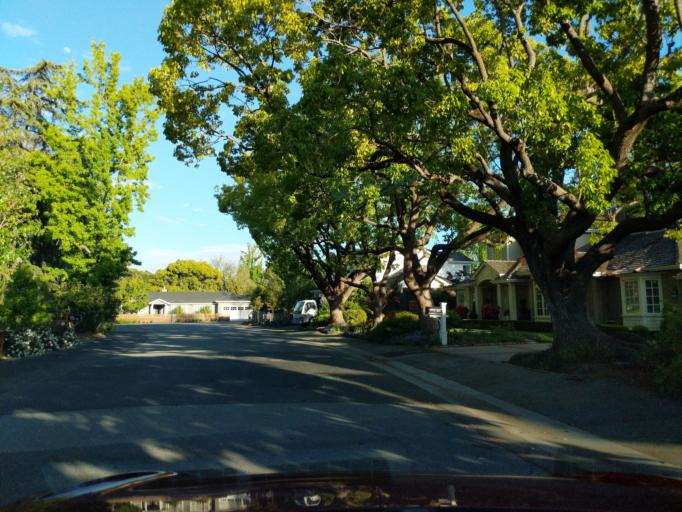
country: US
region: California
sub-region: San Mateo County
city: West Menlo Park
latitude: 37.4323
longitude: -122.1935
